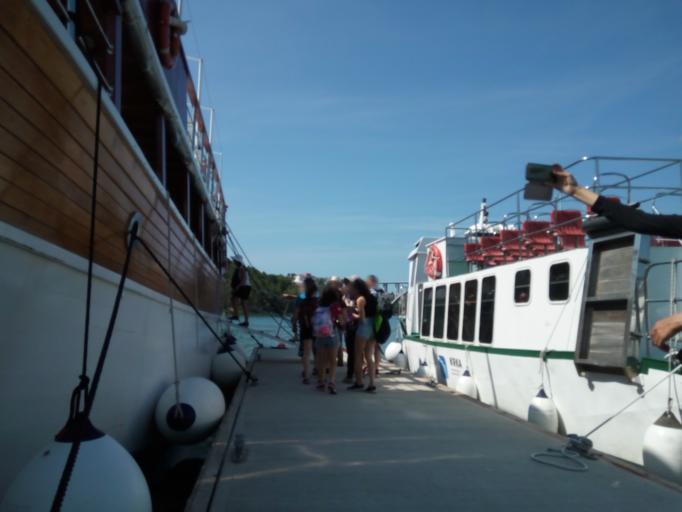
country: HR
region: Sibensko-Kniniska
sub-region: Grad Sibenik
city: Sibenik
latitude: 43.8164
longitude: 15.9227
